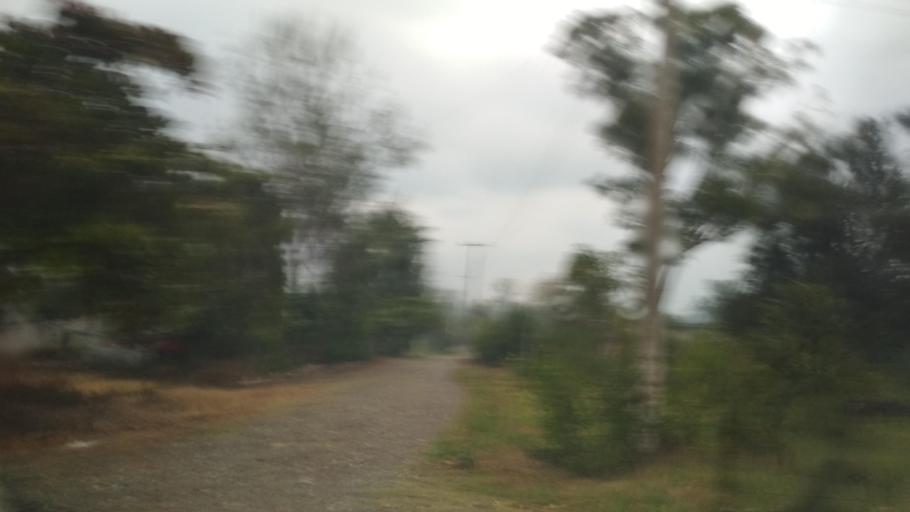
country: MM
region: Shan
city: Taunggyi
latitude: 20.3055
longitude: 97.3033
